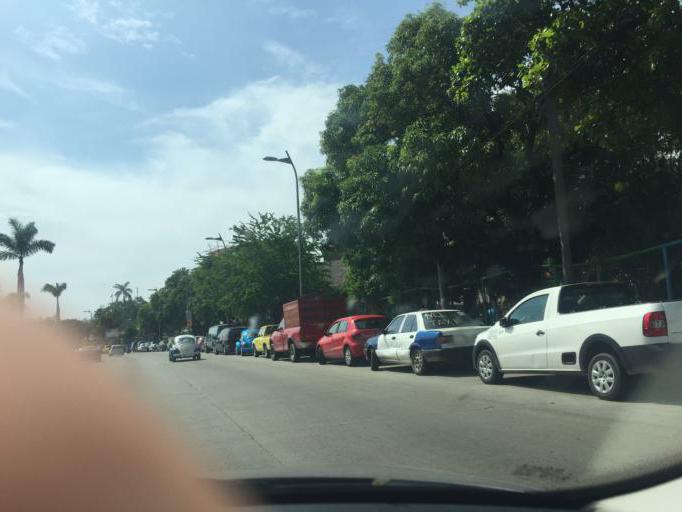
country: MX
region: Guerrero
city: Acapulco de Juarez
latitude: 16.8603
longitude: -99.8845
